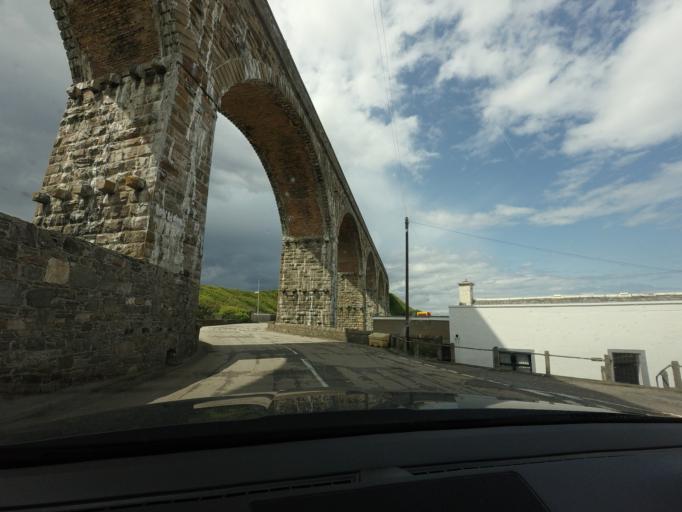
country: GB
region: Scotland
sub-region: Moray
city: Cullen
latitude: 57.6919
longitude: -2.8294
